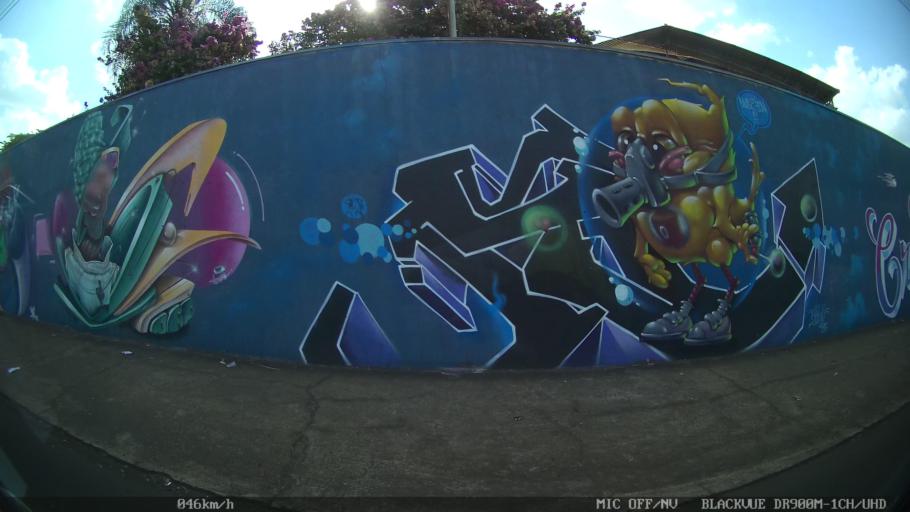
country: BR
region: Sao Paulo
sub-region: Ribeirao Preto
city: Ribeirao Preto
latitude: -21.1770
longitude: -47.8233
